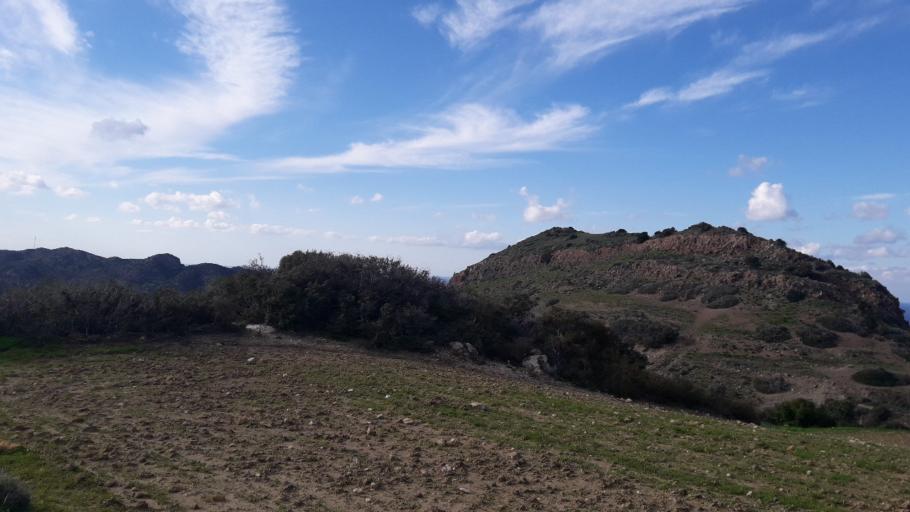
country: CY
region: Ammochostos
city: Leonarisso
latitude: 35.4917
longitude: 34.1375
